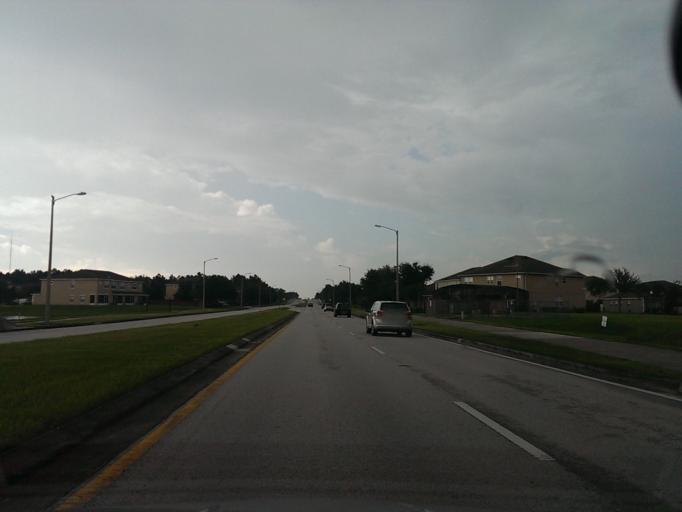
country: US
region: Florida
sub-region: Orange County
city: Winter Garden
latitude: 28.5389
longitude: -81.5834
